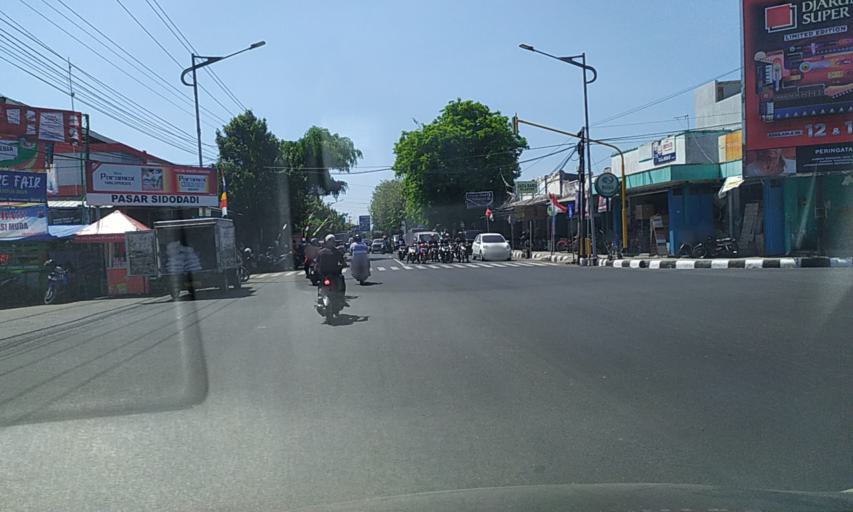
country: ID
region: Central Java
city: Karangbadar Kidul
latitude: -7.7208
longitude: 109.0111
